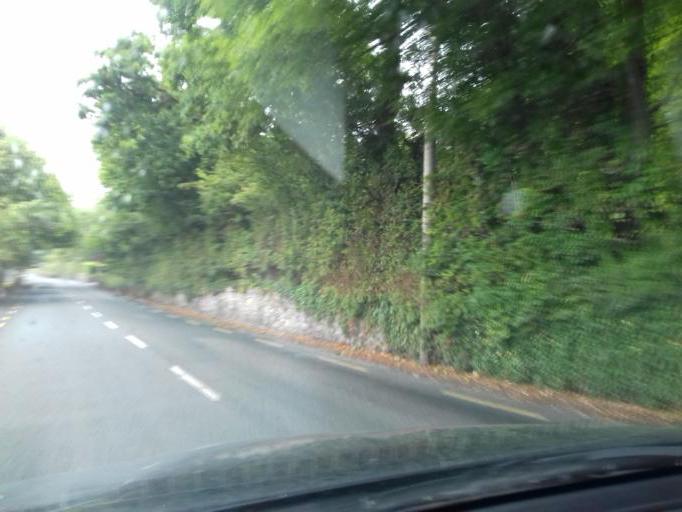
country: IE
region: Leinster
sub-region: County Carlow
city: Bagenalstown
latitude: 52.7092
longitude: -6.9537
